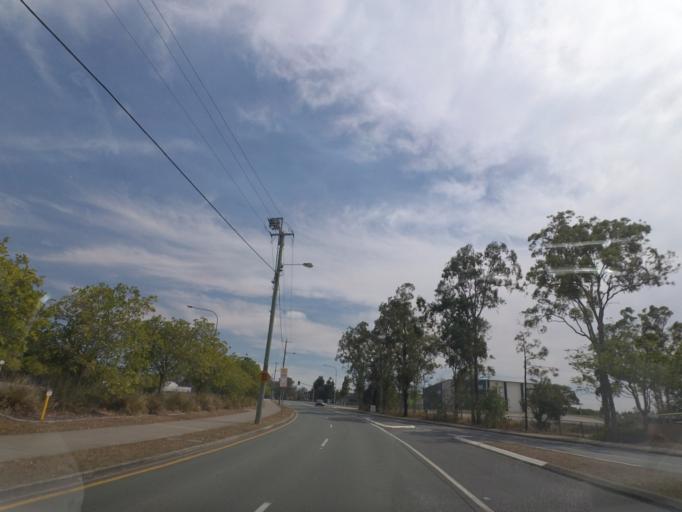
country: AU
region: Queensland
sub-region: Brisbane
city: Sunnybank Hills
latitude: -27.6376
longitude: 153.0574
